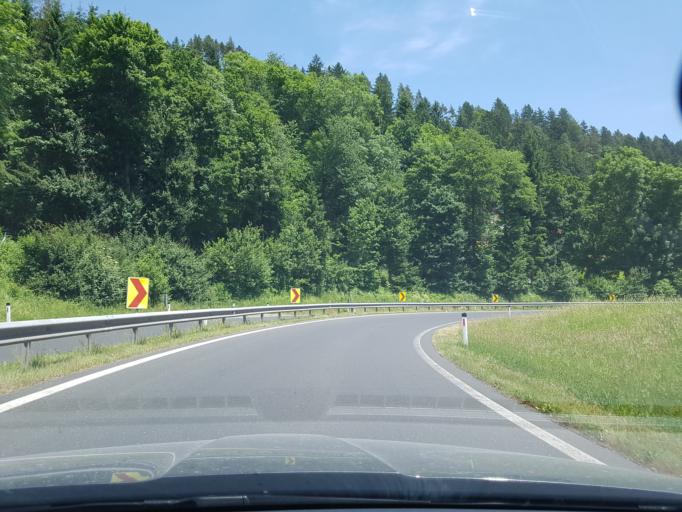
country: AT
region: Carinthia
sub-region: Politischer Bezirk Spittal an der Drau
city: Millstatt
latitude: 46.7821
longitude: 13.5420
